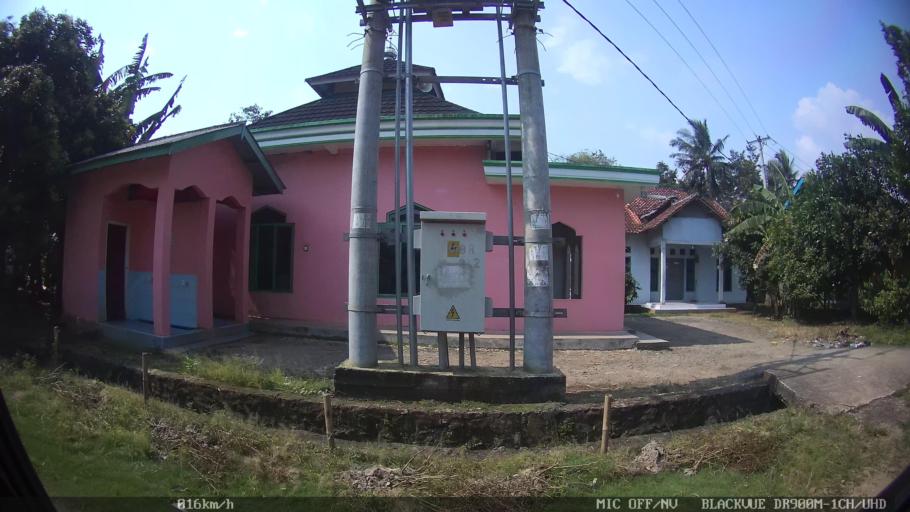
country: ID
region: Lampung
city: Natar
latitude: -5.2951
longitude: 105.2349
